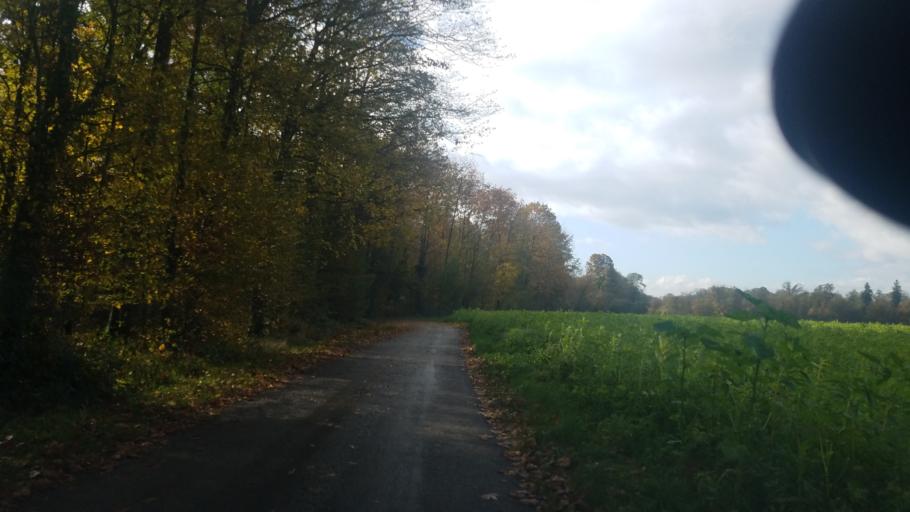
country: DE
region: Baden-Wuerttemberg
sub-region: Freiburg Region
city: Rheinau
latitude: 48.6764
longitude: 7.9803
